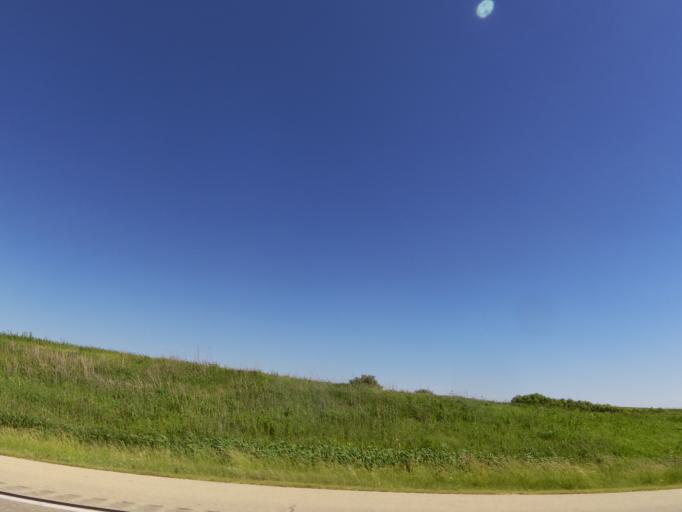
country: US
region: Illinois
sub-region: LaSalle County
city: Earlville
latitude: 41.6974
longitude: -89.0331
